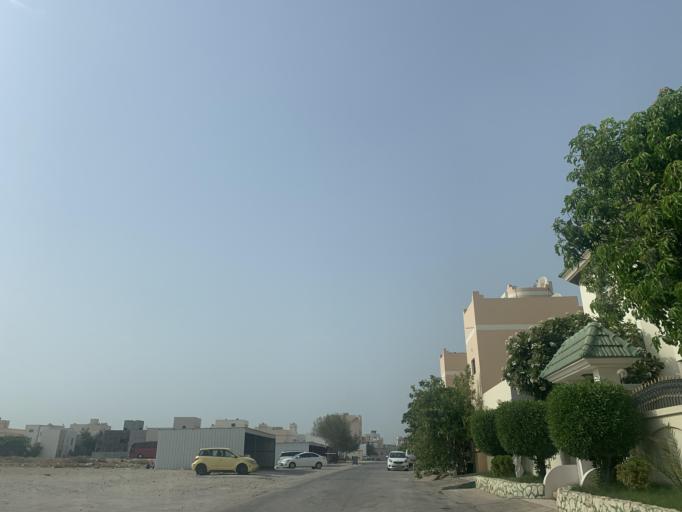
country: BH
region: Northern
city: Madinat `Isa
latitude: 26.1854
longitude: 50.4872
